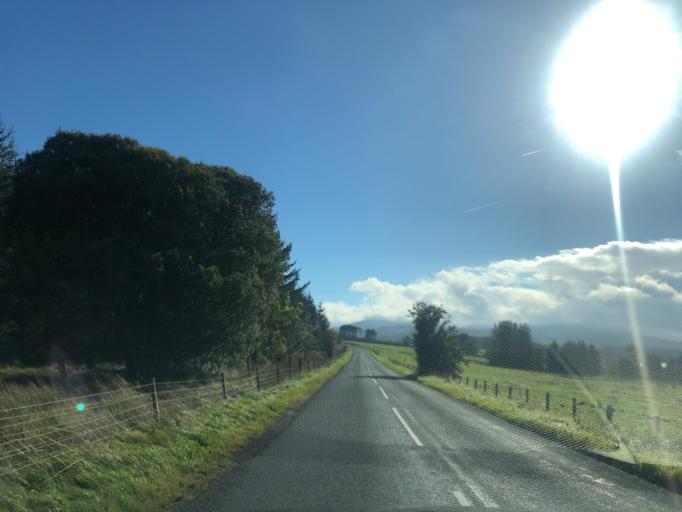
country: GB
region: England
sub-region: Cumbria
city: Keswick
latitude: 54.6252
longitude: -2.9500
